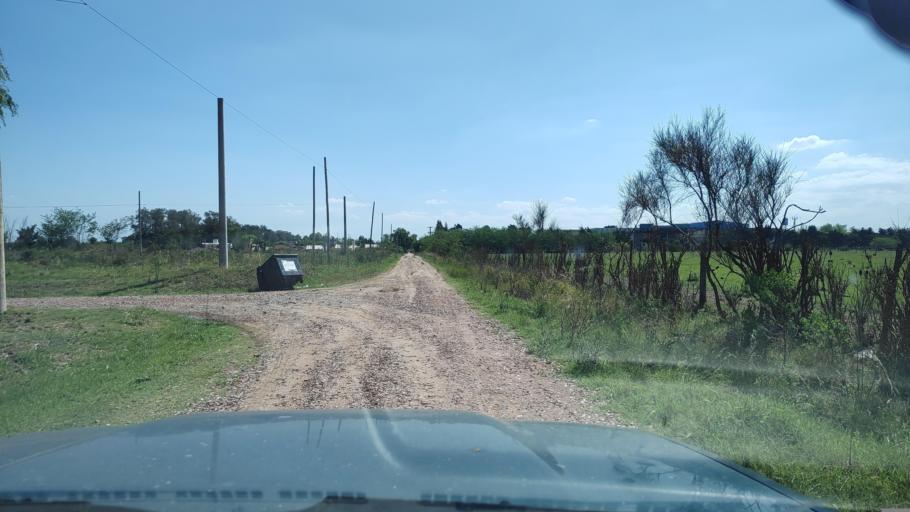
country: AR
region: Buenos Aires
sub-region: Partido de Lujan
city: Lujan
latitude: -34.5653
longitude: -59.1380
